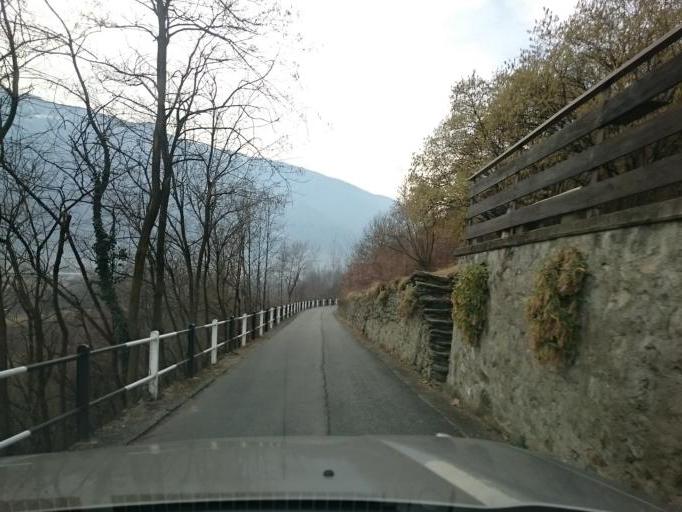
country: IT
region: Lombardy
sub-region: Provincia di Sondrio
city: Vervio
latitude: 46.2490
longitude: 10.2374
